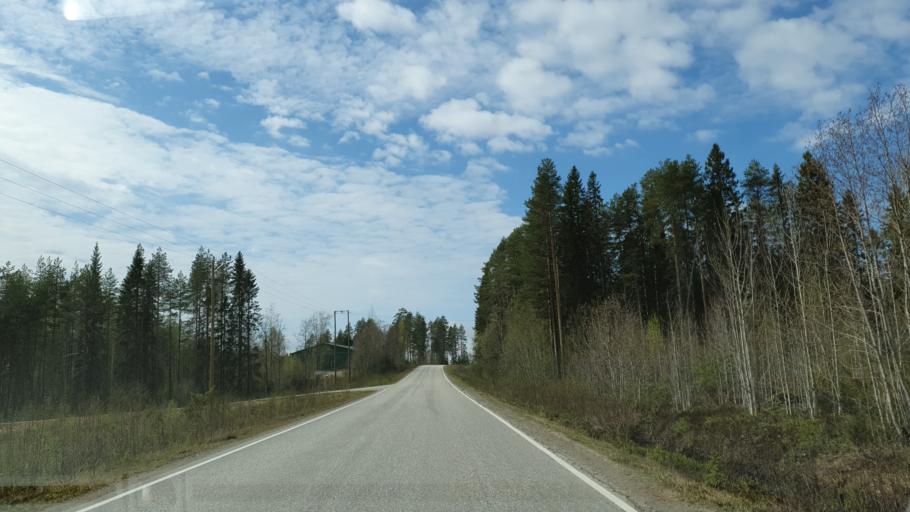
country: FI
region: Kainuu
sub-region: Kehys-Kainuu
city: Kuhmo
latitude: 64.1215
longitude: 29.6725
